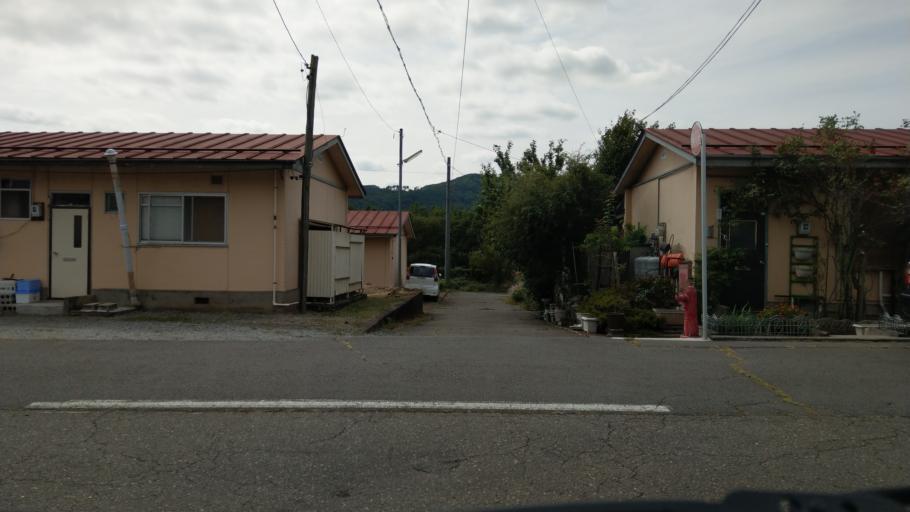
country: JP
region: Nagano
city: Komoro
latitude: 36.3354
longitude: 138.4039
